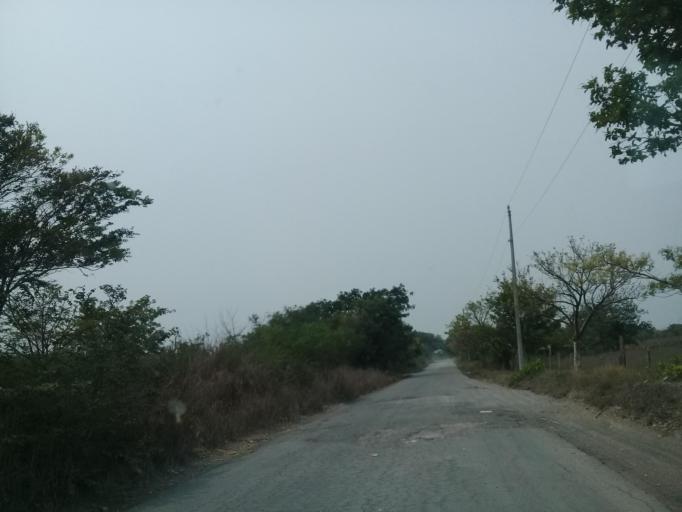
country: MX
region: Veracruz
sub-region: Medellin
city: La Laguna y Monte del Castillo
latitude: 18.9430
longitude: -96.1261
